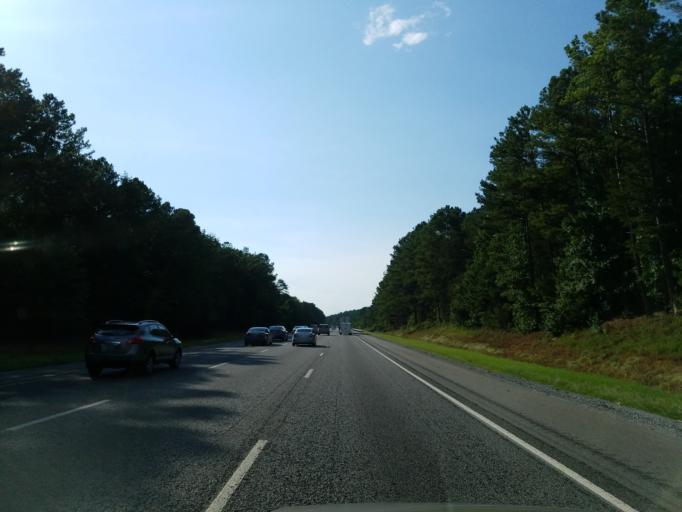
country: US
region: Georgia
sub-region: Bartow County
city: Cartersville
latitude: 34.2362
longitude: -84.7577
